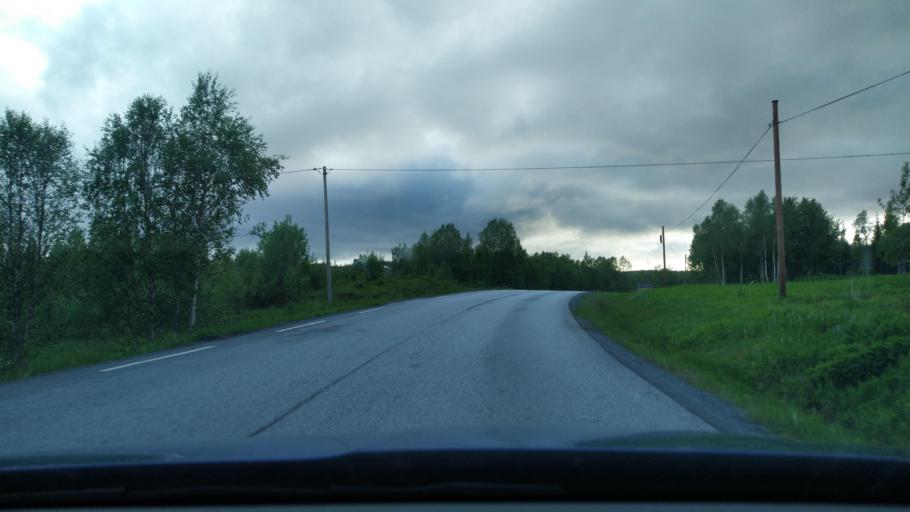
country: NO
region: Troms
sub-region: Dyroy
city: Brostadbotn
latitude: 69.0552
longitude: 17.7938
